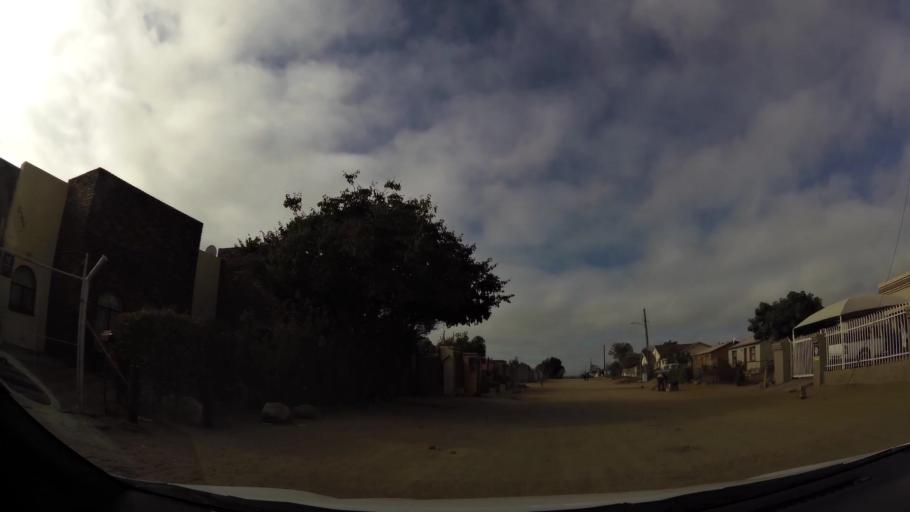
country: ZA
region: Limpopo
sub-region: Capricorn District Municipality
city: Polokwane
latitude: -23.8486
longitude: 29.3829
